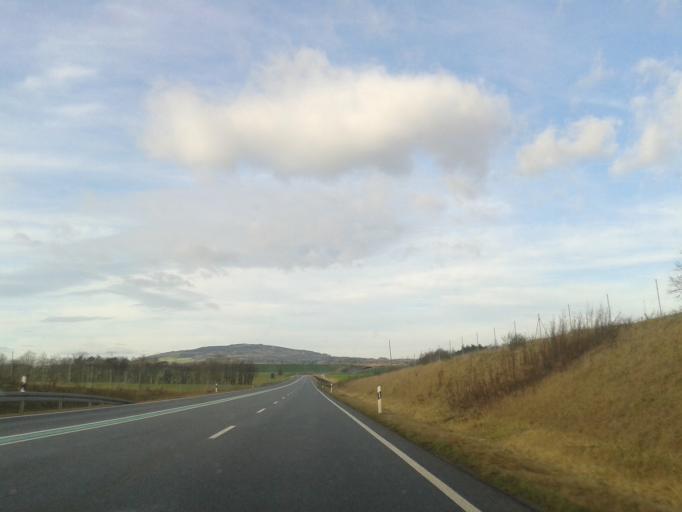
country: DE
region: Saxony
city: Grosshennersdorf
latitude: 50.9684
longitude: 14.7443
